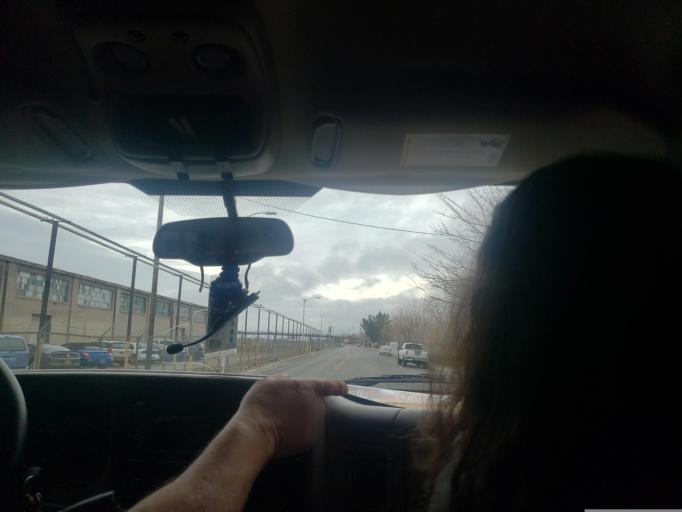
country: US
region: New Mexico
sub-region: Bernalillo County
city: Albuquerque
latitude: 35.0739
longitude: -106.6515
